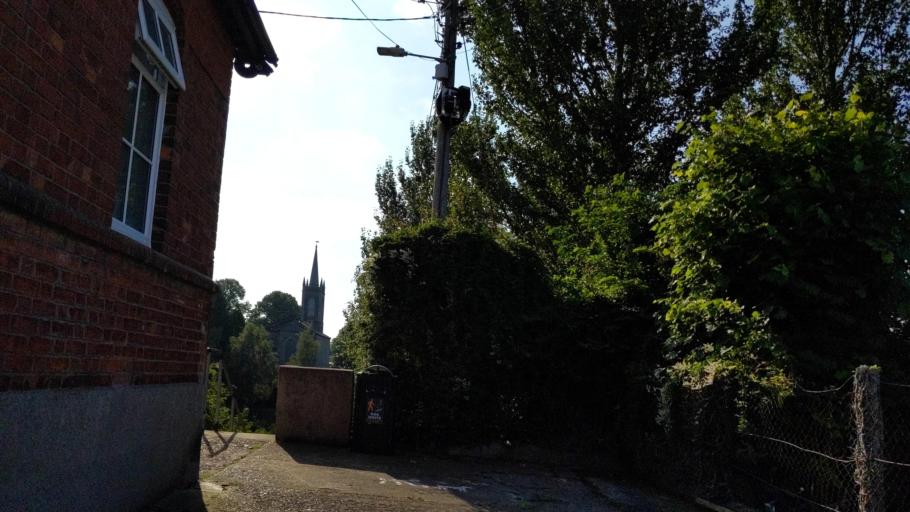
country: IE
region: Leinster
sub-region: Lu
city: Drogheda
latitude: 53.7107
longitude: -6.3451
